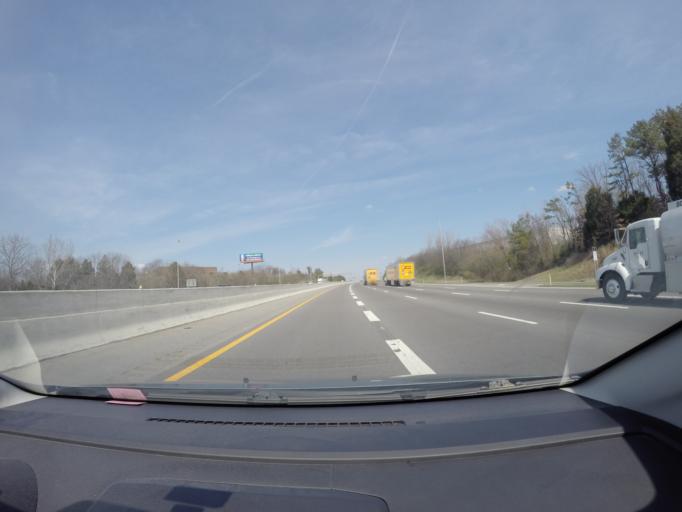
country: US
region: Tennessee
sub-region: Davidson County
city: Oak Hill
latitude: 36.0706
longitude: -86.6902
